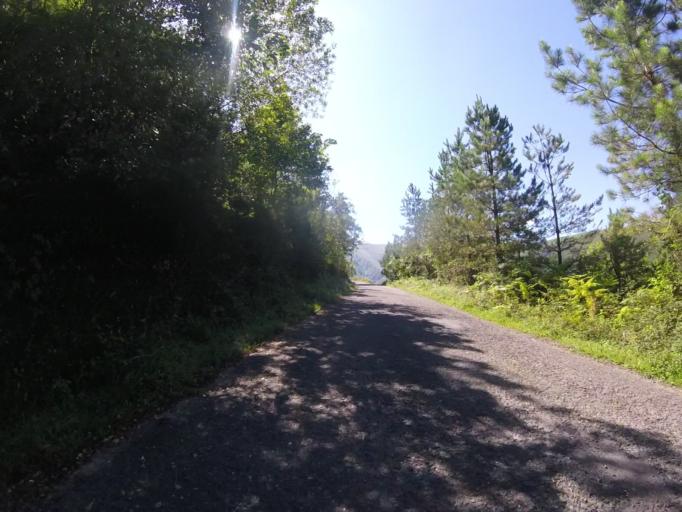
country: ES
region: Navarre
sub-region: Provincia de Navarra
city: Goizueta
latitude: 43.1826
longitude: -1.8255
